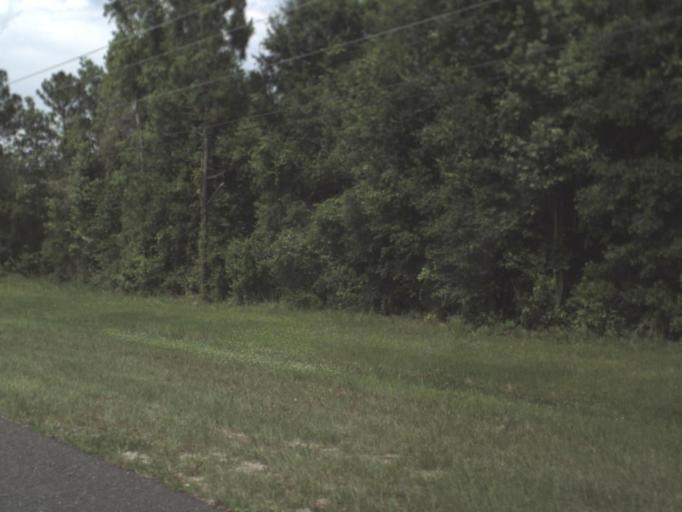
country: US
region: Florida
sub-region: Clay County
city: Green Cove Springs
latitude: 29.8990
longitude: -81.6728
